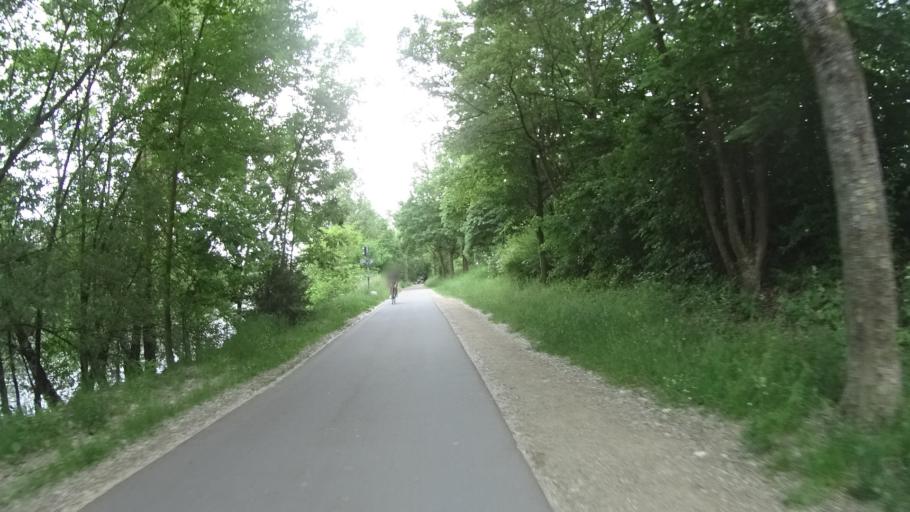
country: DE
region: Bavaria
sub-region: Upper Palatinate
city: Lappersdorf
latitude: 49.0260
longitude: 12.0777
